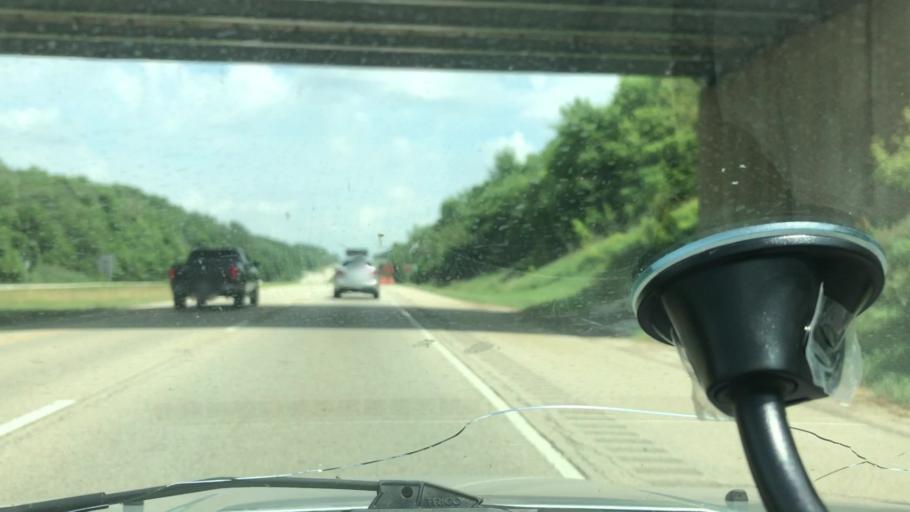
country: US
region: Illinois
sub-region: Peoria County
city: Bellevue
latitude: 40.6843
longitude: -89.6753
